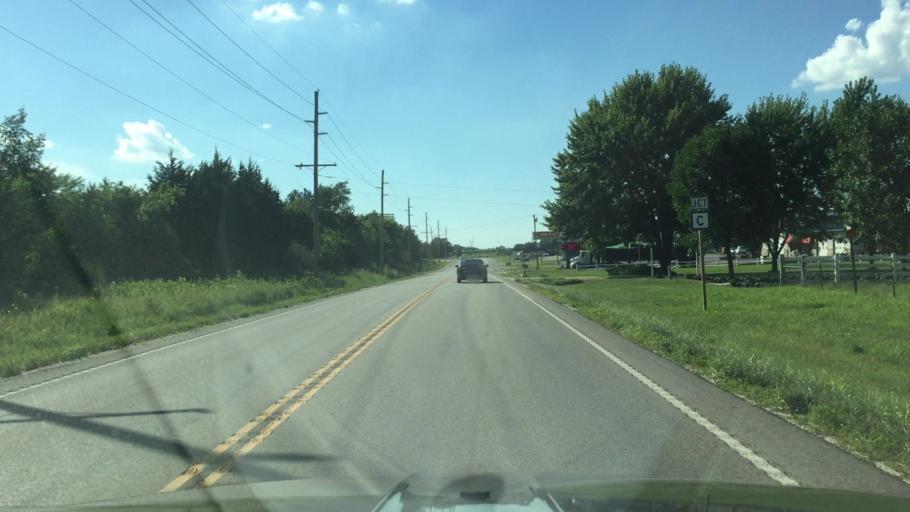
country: US
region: Missouri
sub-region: Morgan County
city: Versailles
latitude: 38.4453
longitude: -92.7927
